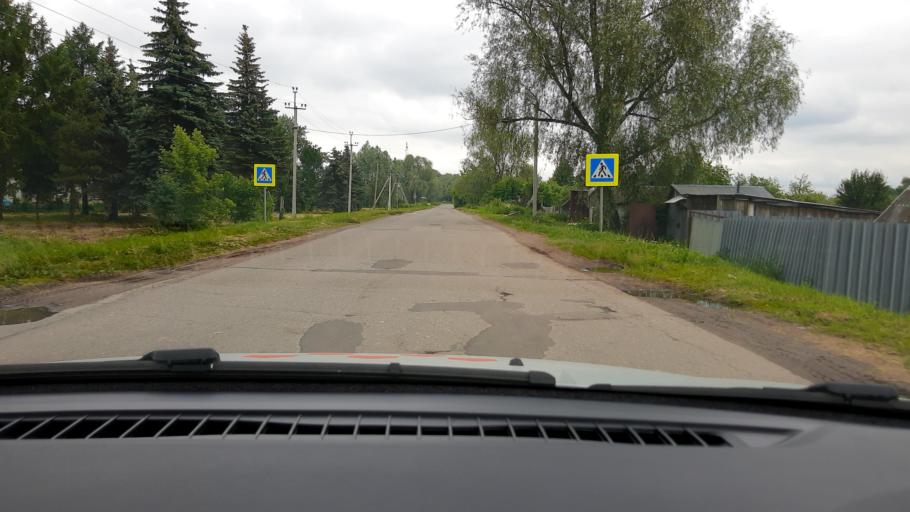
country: RU
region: Nizjnij Novgorod
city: Bogorodsk
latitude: 56.0717
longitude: 43.5060
